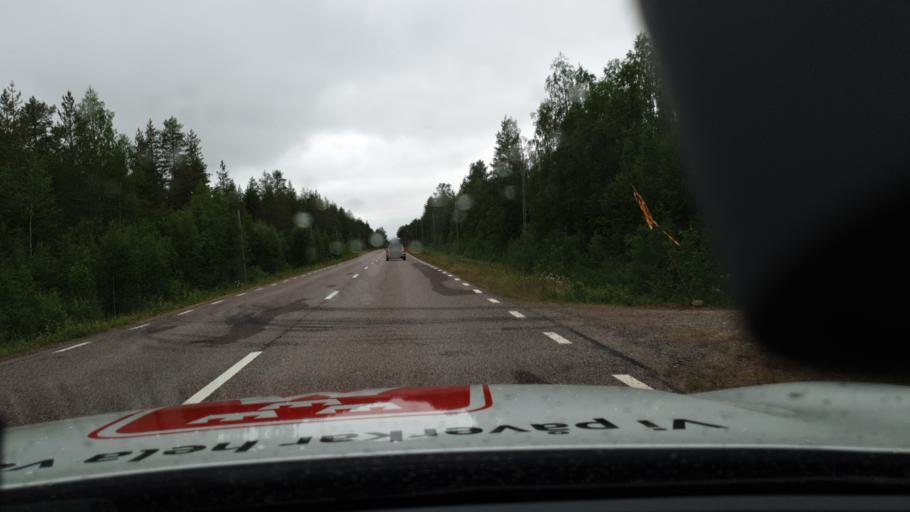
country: FI
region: Lapland
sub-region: Torniolaakso
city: Pello
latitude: 66.9737
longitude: 23.8098
